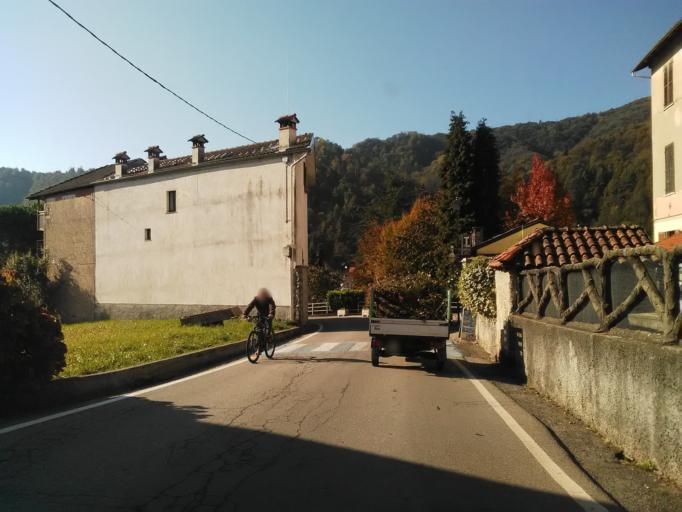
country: IT
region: Piedmont
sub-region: Provincia di Vercelli
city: Postua
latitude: 45.7131
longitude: 8.2304
